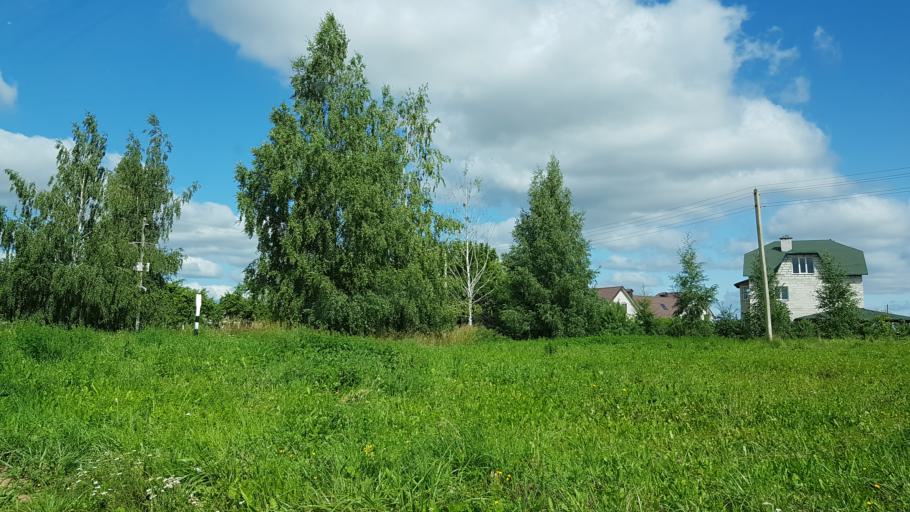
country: BY
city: Fanipol
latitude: 53.7543
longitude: 27.3247
